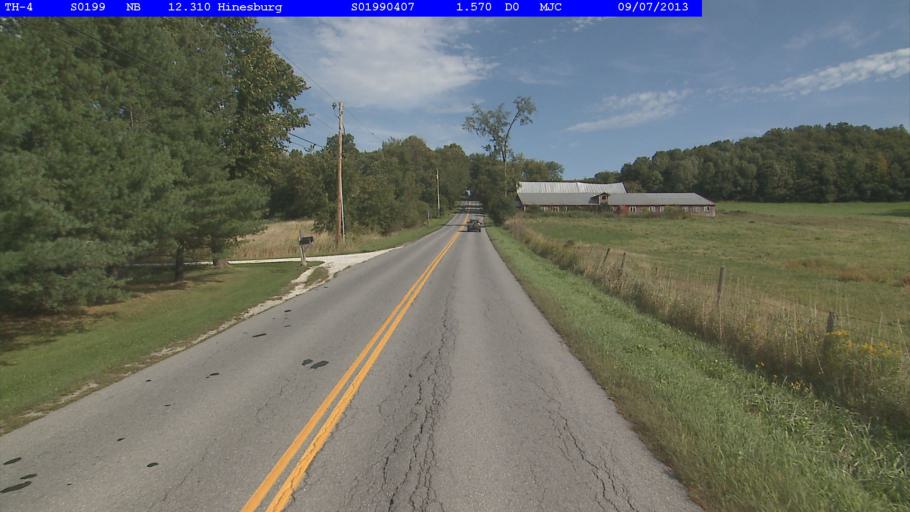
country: US
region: Vermont
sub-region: Chittenden County
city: Hinesburg
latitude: 44.3006
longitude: -73.1095
